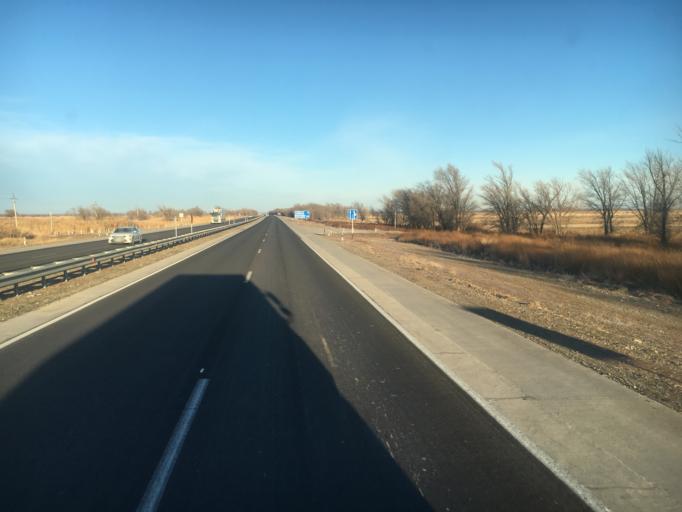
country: KZ
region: Ongtustik Qazaqstan
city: Bayaldyr
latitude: 43.0933
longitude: 68.6371
